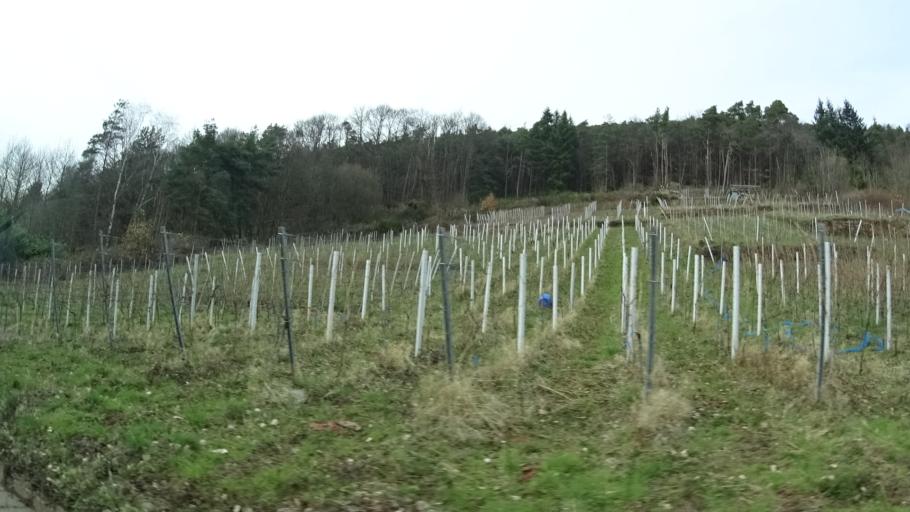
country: DE
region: Rheinland-Pfalz
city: Sankt Martin
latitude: 49.3018
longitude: 8.0960
